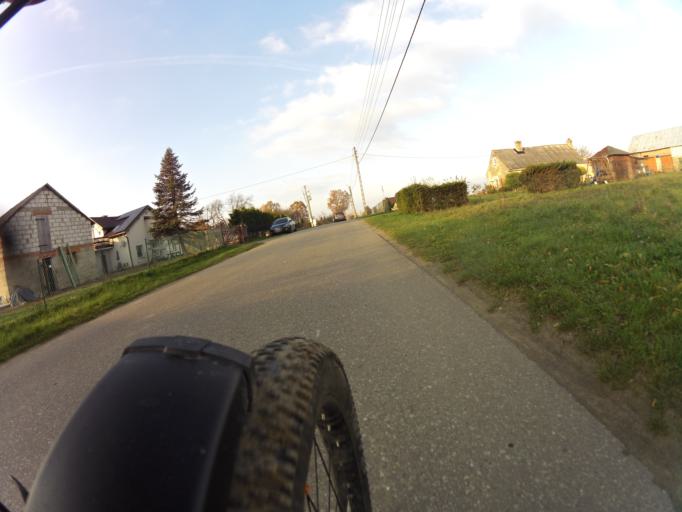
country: PL
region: Pomeranian Voivodeship
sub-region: Powiat pucki
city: Krokowa
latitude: 54.7656
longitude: 18.1808
